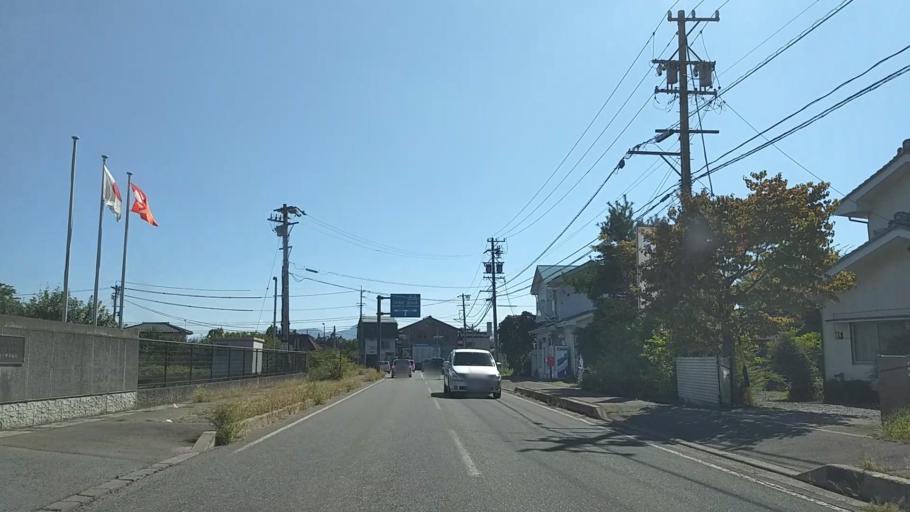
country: JP
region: Nagano
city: Nagano-shi
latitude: 36.6173
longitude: 138.1414
